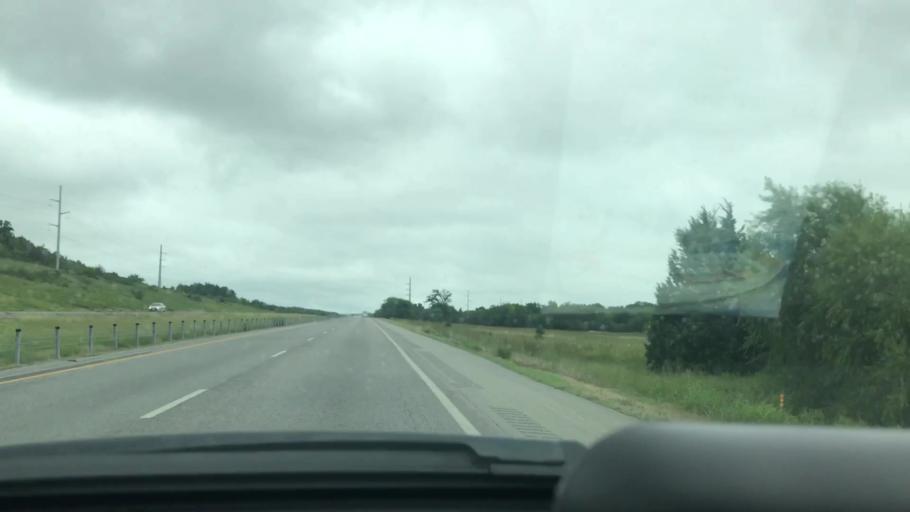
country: US
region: Oklahoma
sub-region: Coal County
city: Coalgate
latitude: 34.6511
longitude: -95.9425
